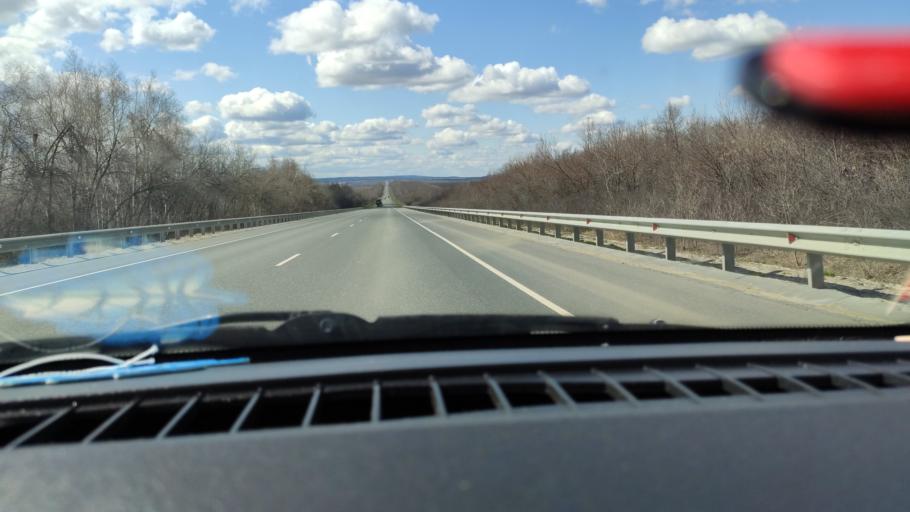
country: RU
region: Saratov
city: Khvalynsk
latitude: 52.6132
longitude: 48.1622
